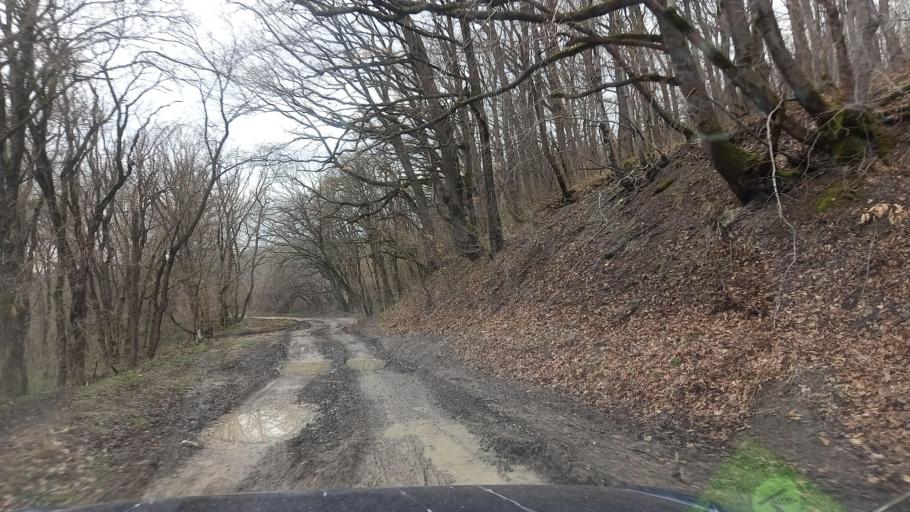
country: RU
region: Krasnodarskiy
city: Novorossiysk
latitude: 44.8573
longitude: 37.8460
